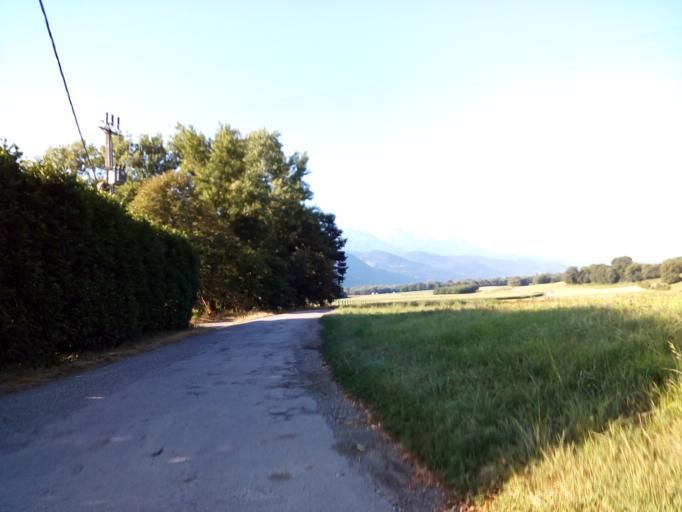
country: FR
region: Rhone-Alpes
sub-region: Departement de l'Isere
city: Saint-Vincent-de-Mercuze
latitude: 45.3761
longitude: 5.9724
